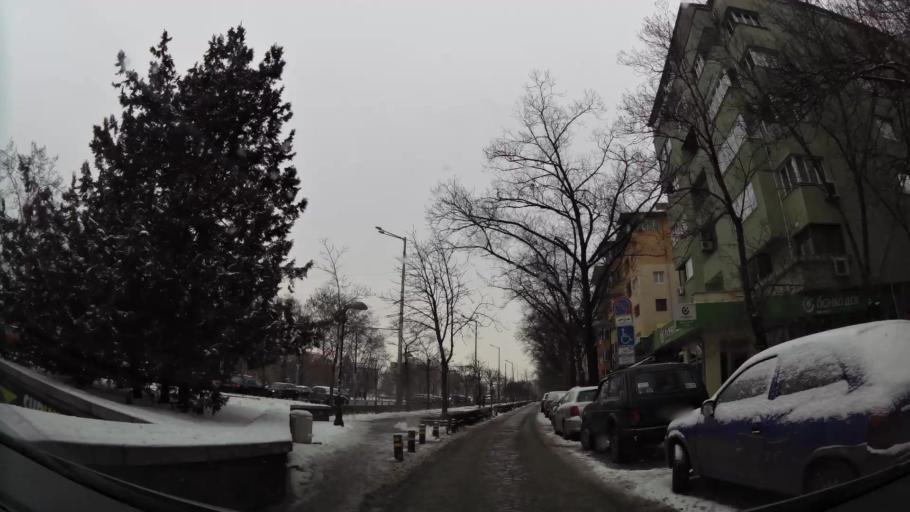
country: BG
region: Sofia-Capital
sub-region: Stolichna Obshtina
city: Sofia
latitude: 42.6910
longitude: 23.3372
